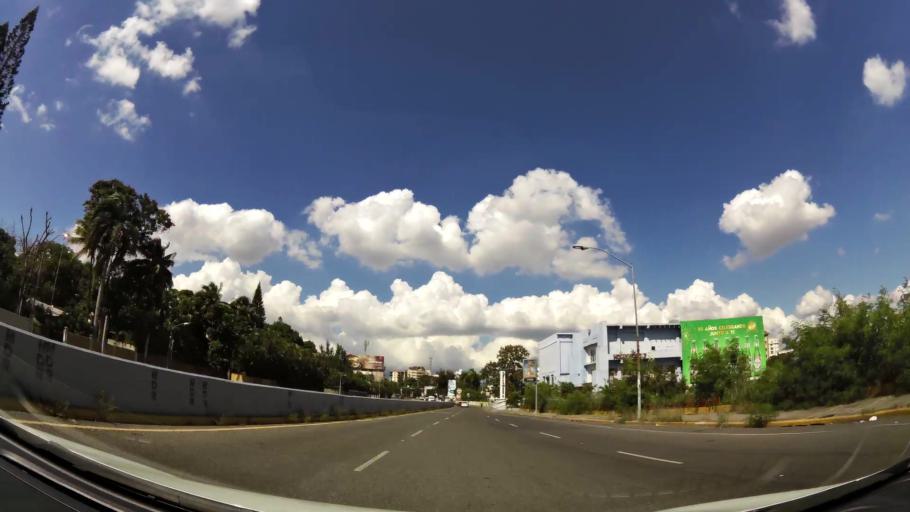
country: DO
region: Santiago
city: Santiago de los Caballeros
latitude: 19.4508
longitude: -70.6860
